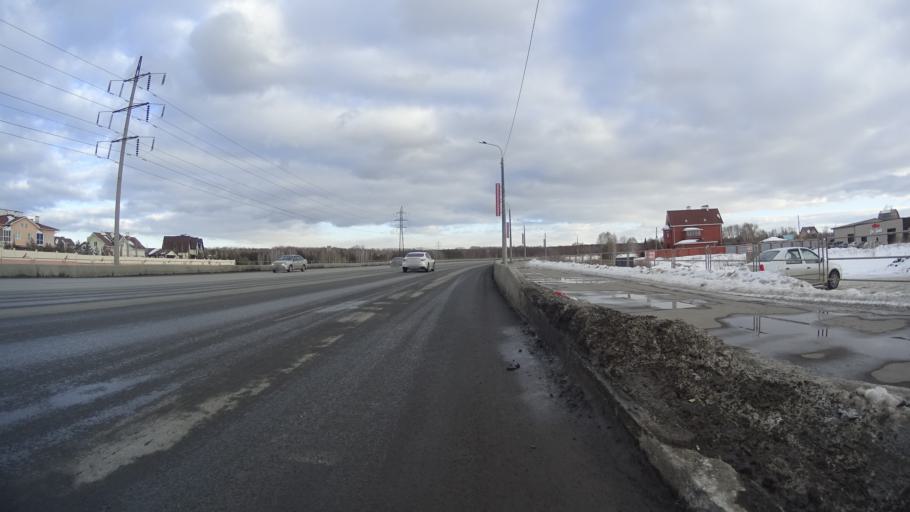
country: RU
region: Chelyabinsk
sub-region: Gorod Chelyabinsk
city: Chelyabinsk
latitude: 55.1546
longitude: 61.3166
